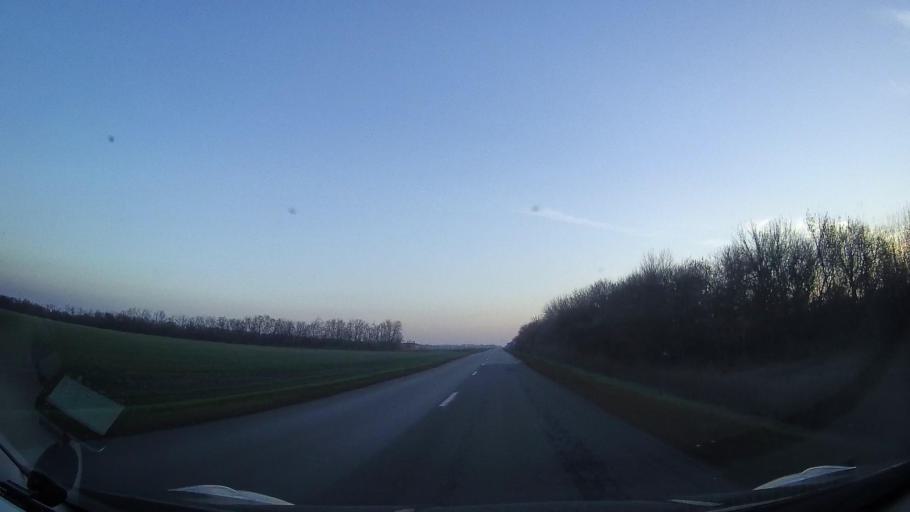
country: RU
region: Rostov
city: Zernograd
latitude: 47.0312
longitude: 40.3917
